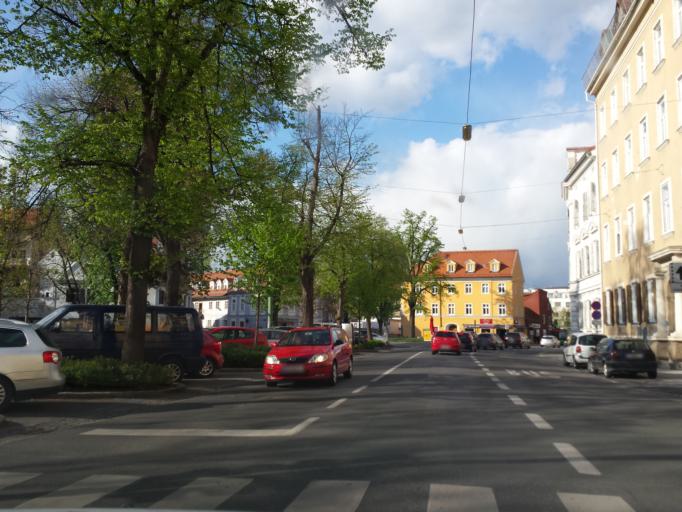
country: AT
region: Styria
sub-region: Graz Stadt
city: Graz
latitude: 47.0737
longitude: 15.4294
